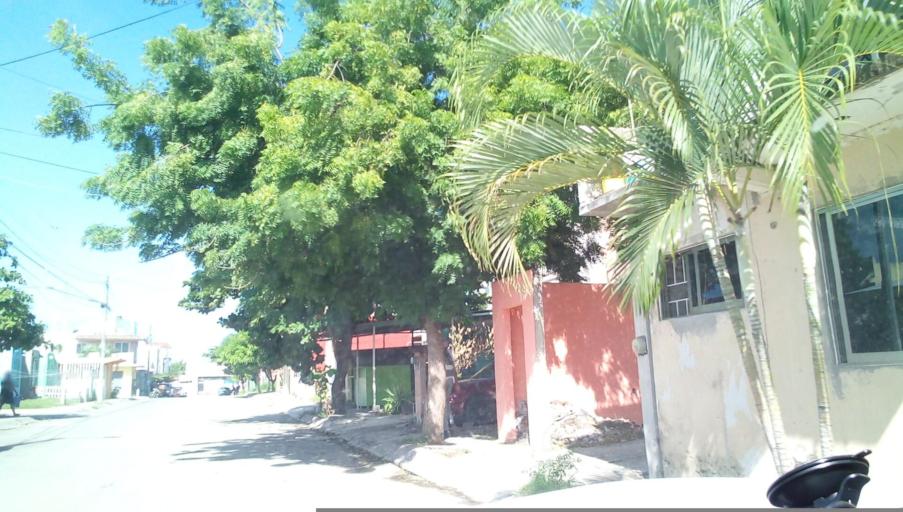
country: MX
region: Veracruz
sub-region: Veracruz
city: Las Amapolas
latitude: 19.1548
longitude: -96.2155
